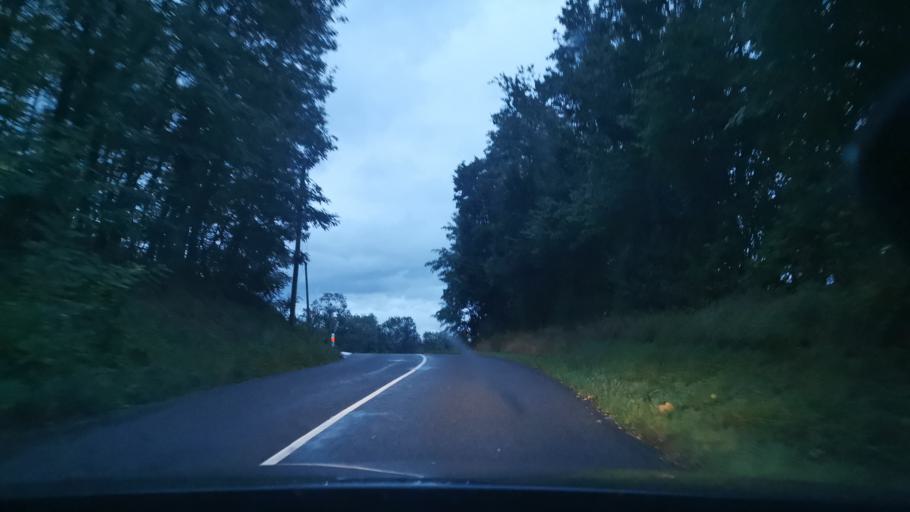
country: FR
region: Rhone-Alpes
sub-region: Departement de l'Ain
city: Pont-de-Veyle
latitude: 46.2650
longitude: 4.8978
